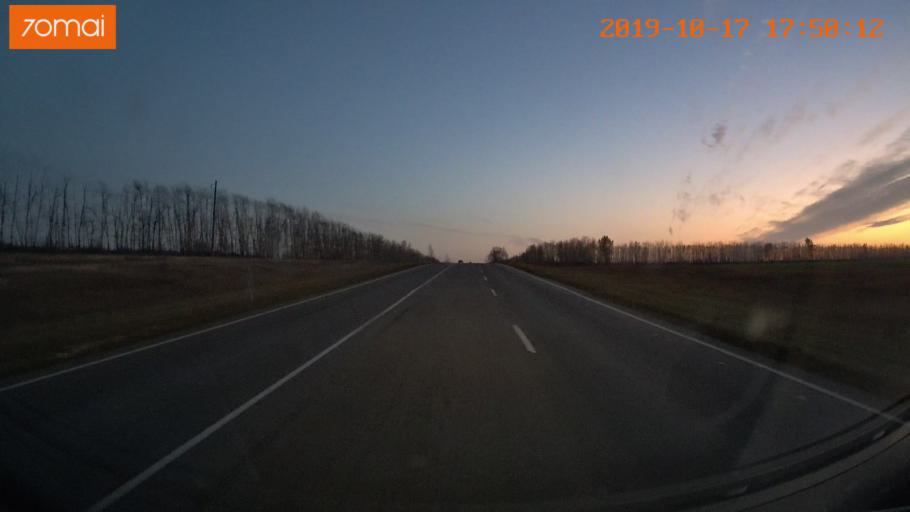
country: RU
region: Tula
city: Yepifan'
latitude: 53.6671
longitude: 38.6880
